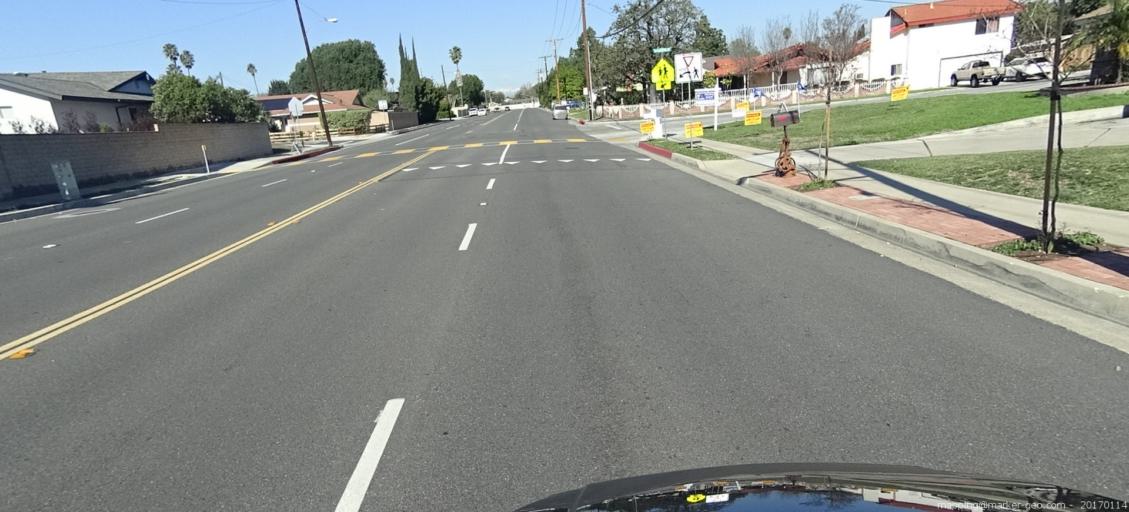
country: US
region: California
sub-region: Orange County
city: Tustin
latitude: 33.7567
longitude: -117.8143
